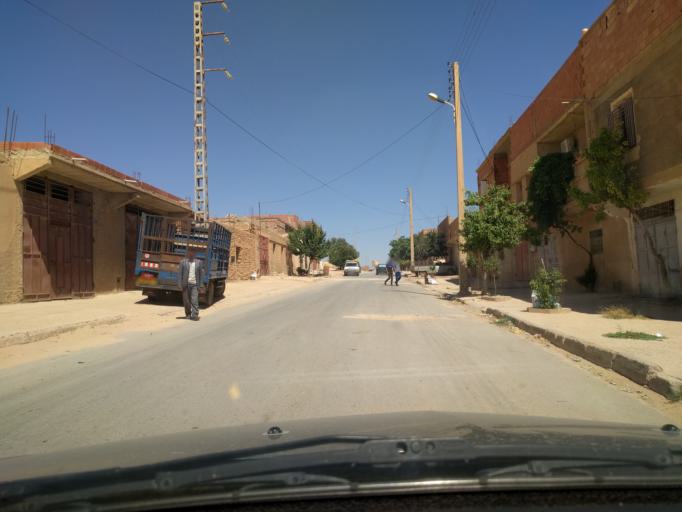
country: DZ
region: Tiaret
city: Frenda
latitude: 34.8908
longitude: 1.2444
